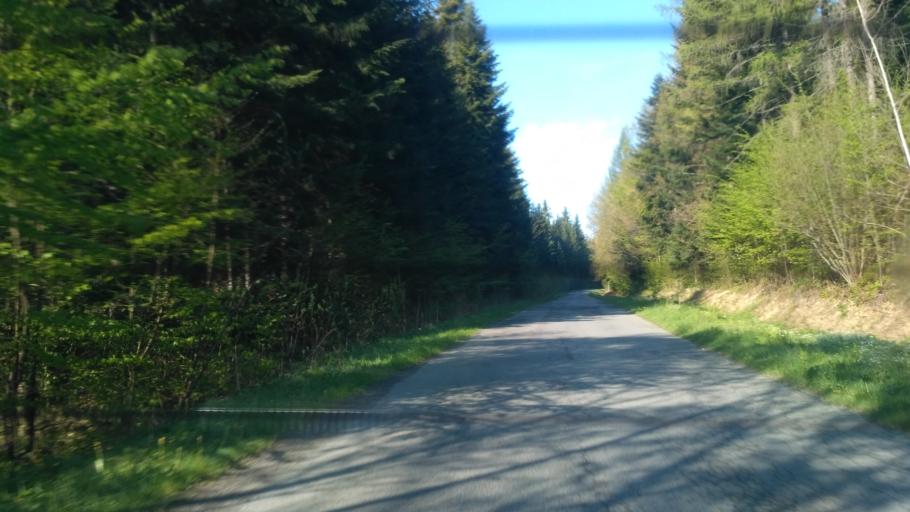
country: PL
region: Subcarpathian Voivodeship
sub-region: Powiat jaroslawski
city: Kramarzowka
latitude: 49.8491
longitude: 22.5316
